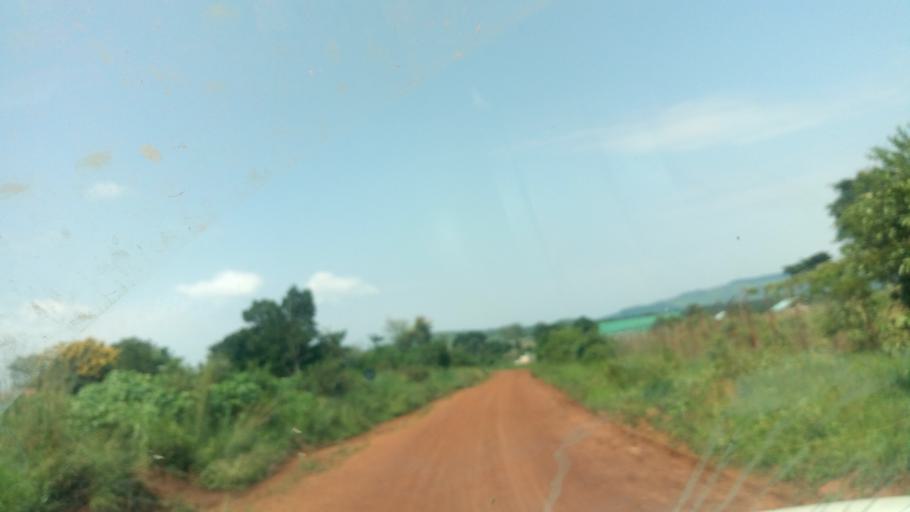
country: UG
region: Western Region
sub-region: Masindi District
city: Masindi
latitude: 1.6767
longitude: 31.8298
